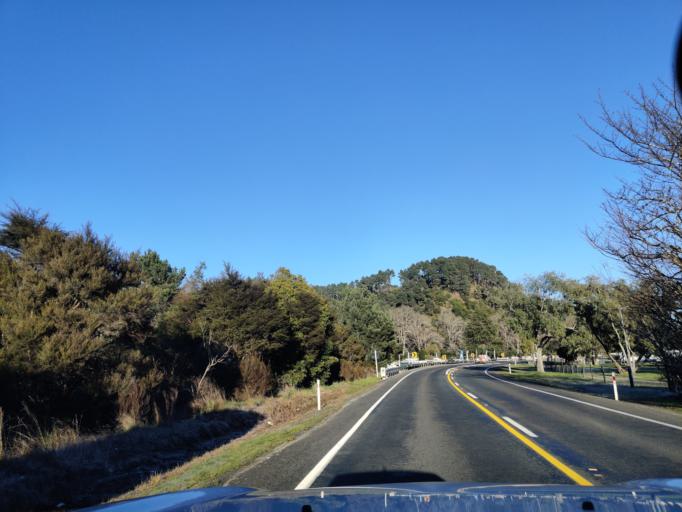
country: NZ
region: Waikato
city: Turangi
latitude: -38.8872
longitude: 175.9607
